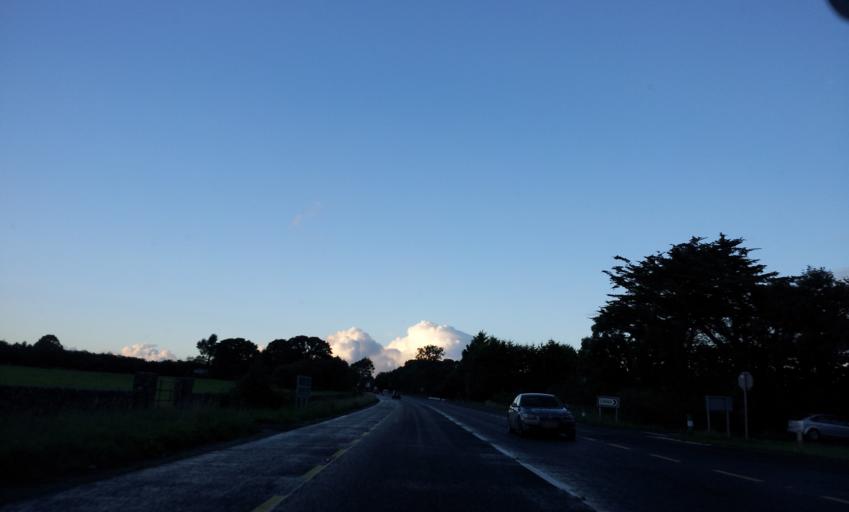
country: IE
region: Munster
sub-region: County Limerick
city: Rathkeale
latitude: 52.5014
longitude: -8.9927
